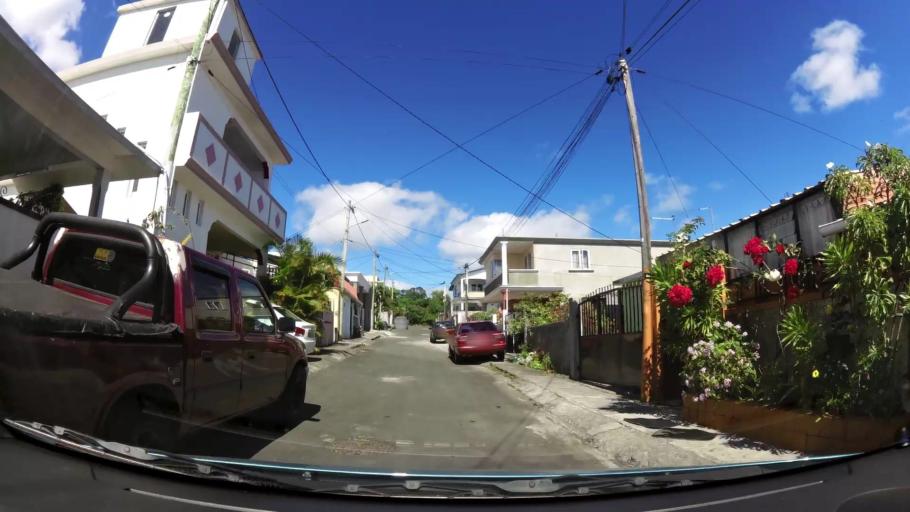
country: MU
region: Plaines Wilhems
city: Vacoas
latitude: -20.3054
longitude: 57.4724
